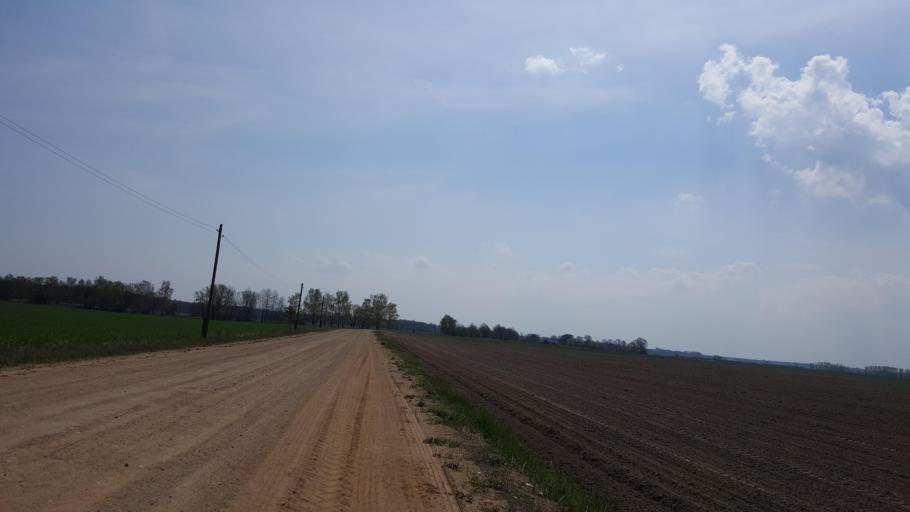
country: BY
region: Brest
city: Zhabinka
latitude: 52.2960
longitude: 23.9146
